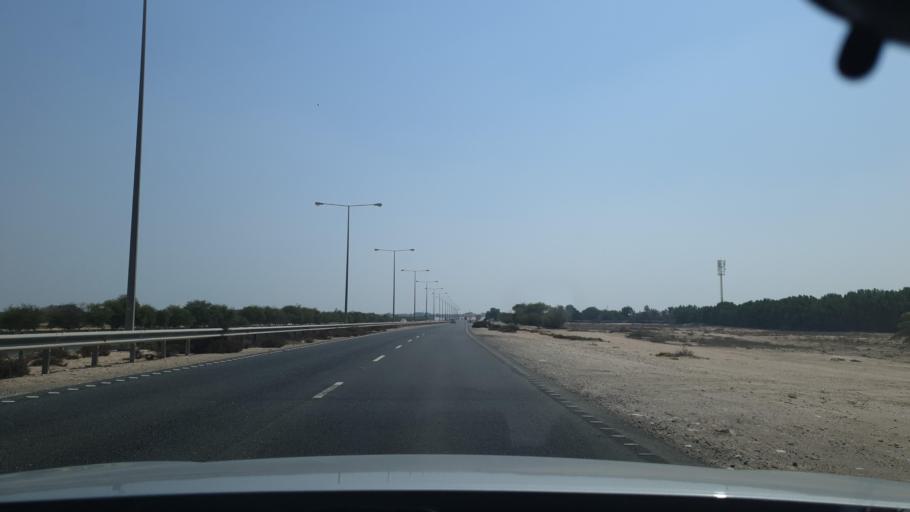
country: QA
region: Al Khawr
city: Al Khawr
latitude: 25.7333
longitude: 51.4933
